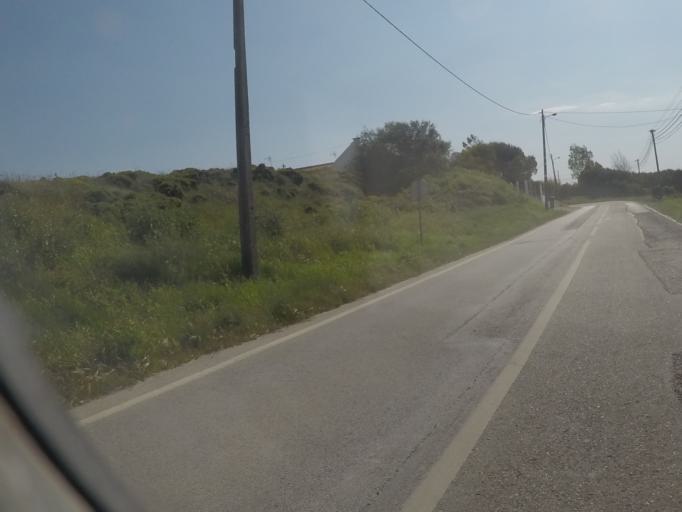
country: PT
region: Setubal
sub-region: Sesimbra
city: Sesimbra
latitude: 38.4450
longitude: -9.1648
